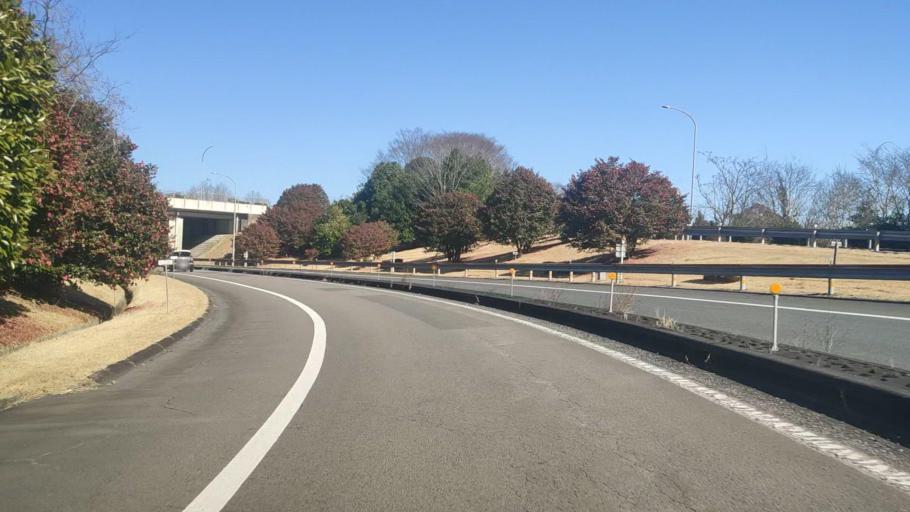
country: JP
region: Miyazaki
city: Miyakonojo
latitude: 31.7812
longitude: 131.1150
